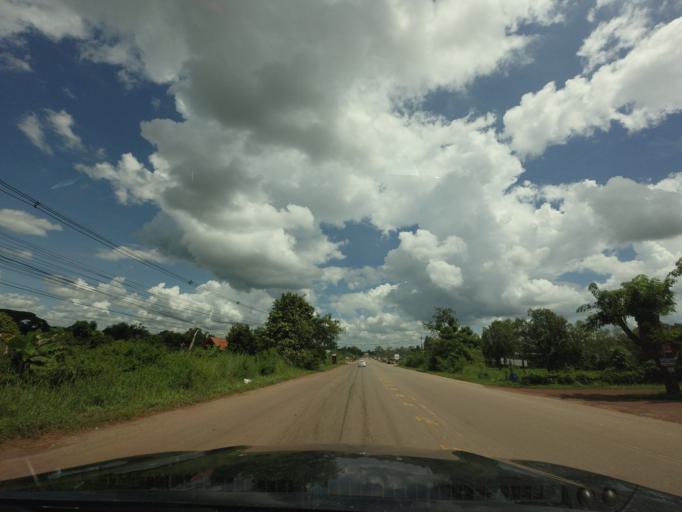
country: TH
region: Changwat Udon Thani
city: Ban Dung
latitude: 17.6792
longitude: 103.2380
